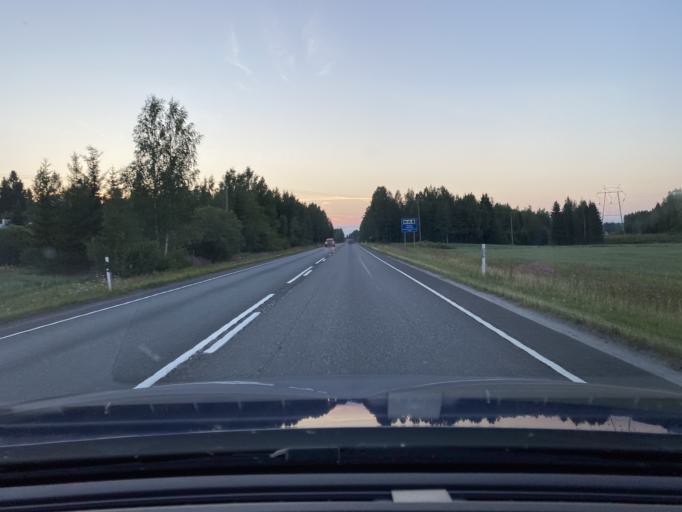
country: FI
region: Pirkanmaa
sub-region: Luoteis-Pirkanmaa
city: Ikaalinen
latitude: 61.8236
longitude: 22.9476
